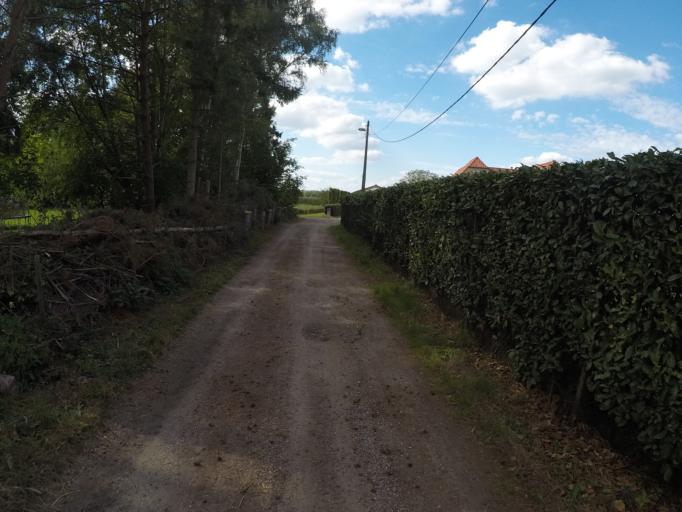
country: BE
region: Flanders
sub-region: Provincie Antwerpen
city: Ranst
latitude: 51.1653
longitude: 4.6077
